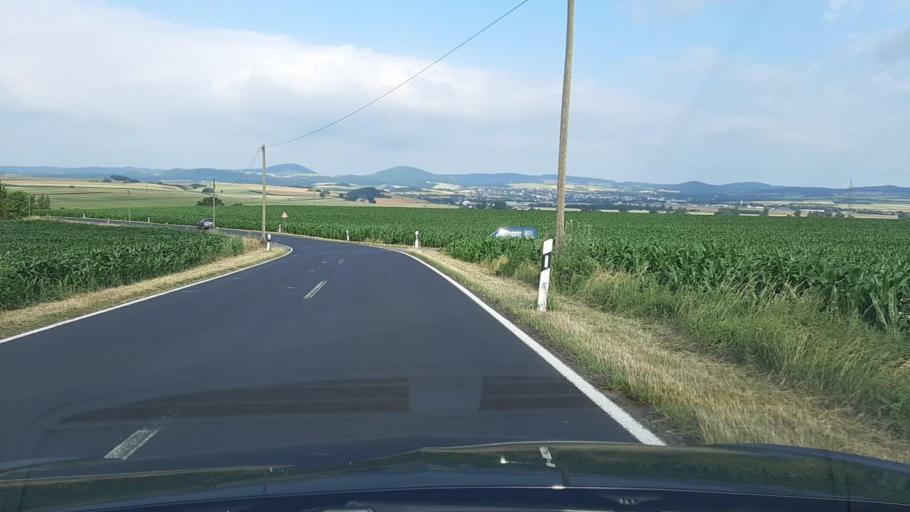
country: DE
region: Rheinland-Pfalz
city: Welling
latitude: 50.3474
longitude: 7.3440
